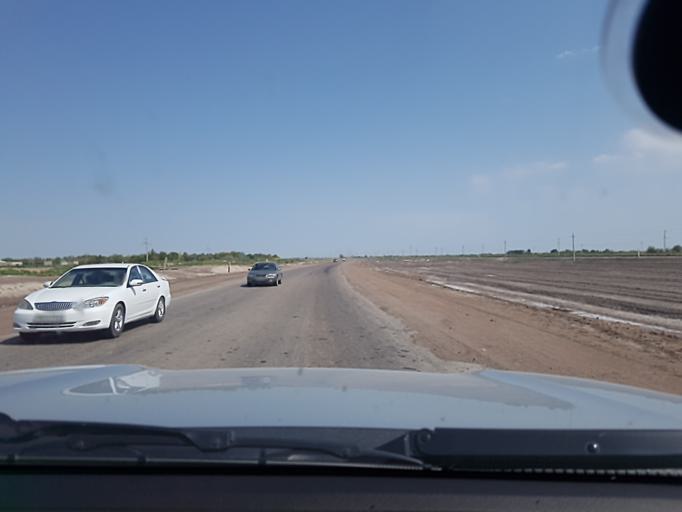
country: TM
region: Dasoguz
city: Koeneuergench
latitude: 42.2667
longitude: 59.3015
